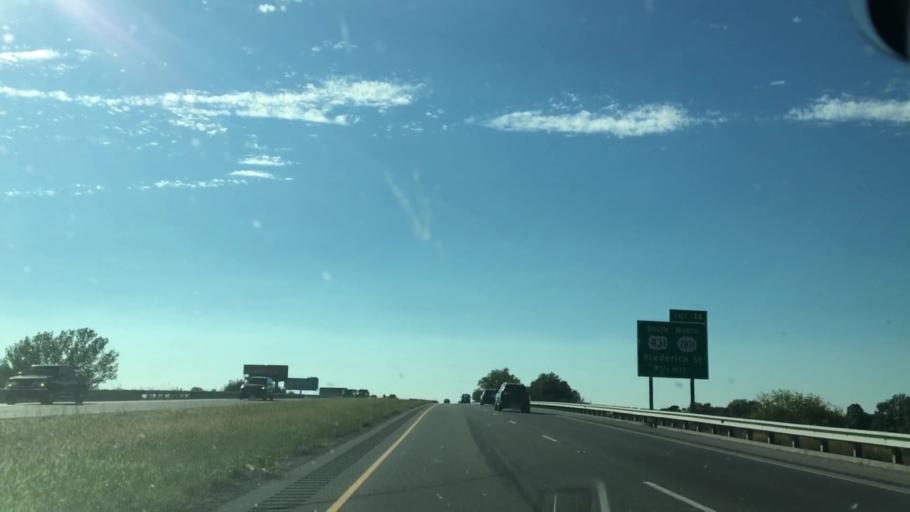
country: US
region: Kentucky
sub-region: Daviess County
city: Owensboro
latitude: 37.7259
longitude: -87.1088
